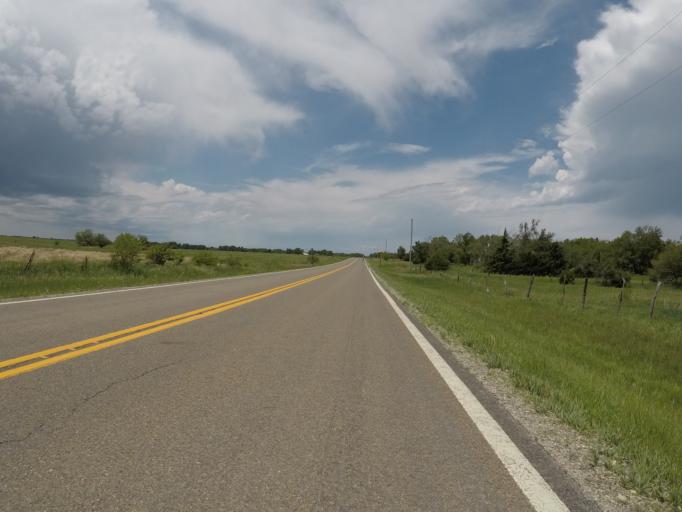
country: US
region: Kansas
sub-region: Wabaunsee County
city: Alma
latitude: 38.8549
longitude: -96.4160
